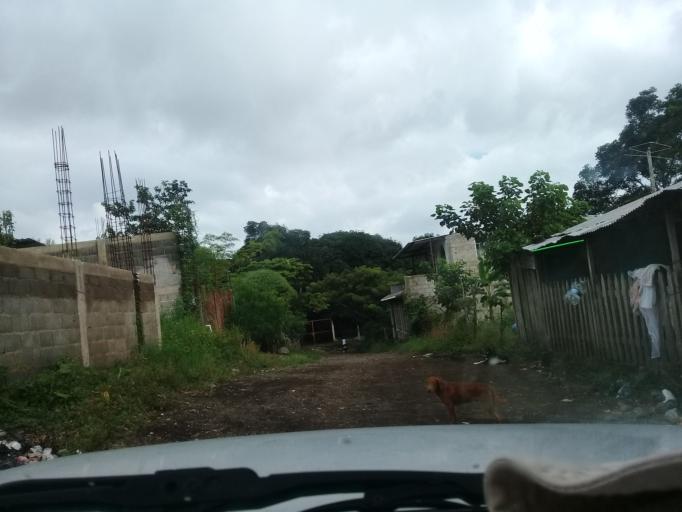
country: MX
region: Veracruz
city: Catemaco
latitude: 18.4302
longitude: -95.1310
